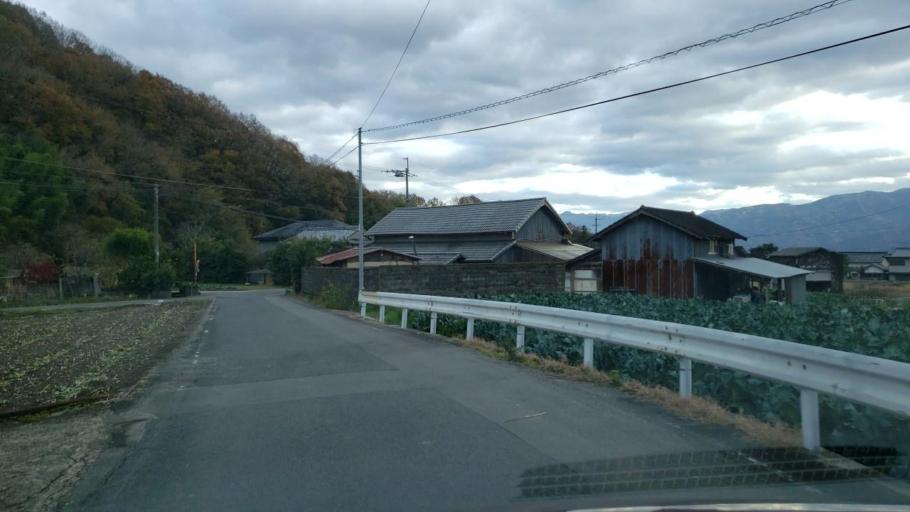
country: JP
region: Tokushima
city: Wakimachi
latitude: 34.1054
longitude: 134.2244
